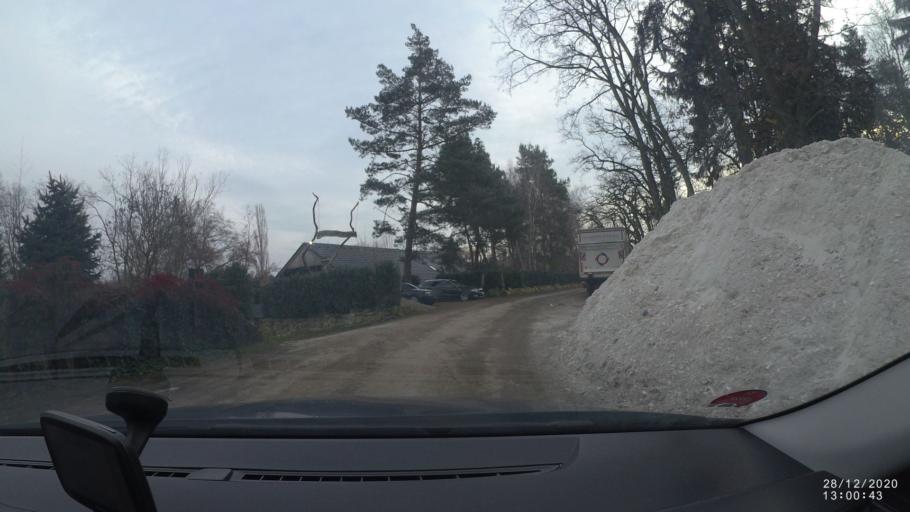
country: CZ
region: Praha
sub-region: Praha 20
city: Horni Pocernice
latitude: 50.1464
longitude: 14.6047
